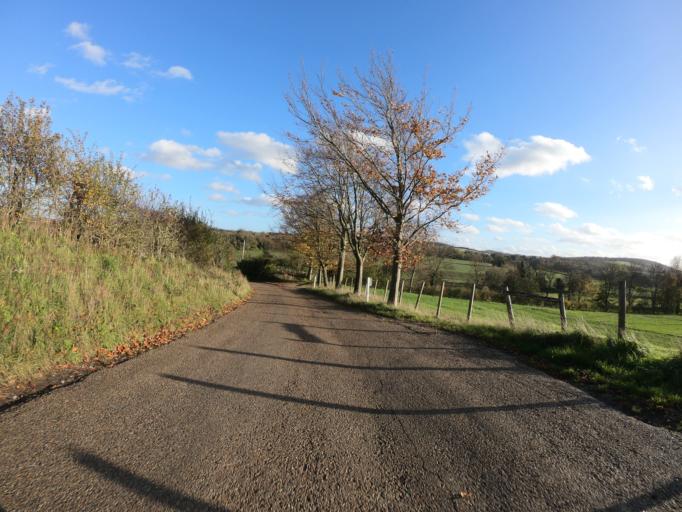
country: GB
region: England
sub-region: Kent
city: Eynsford
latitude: 51.3676
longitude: 0.1983
